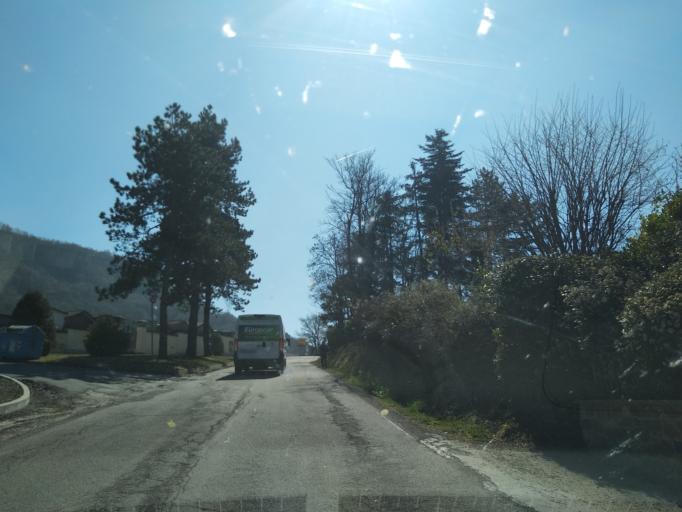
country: IT
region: Emilia-Romagna
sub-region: Provincia di Reggio Emilia
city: Castelnovo ne'Monti
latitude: 44.4310
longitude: 10.4077
